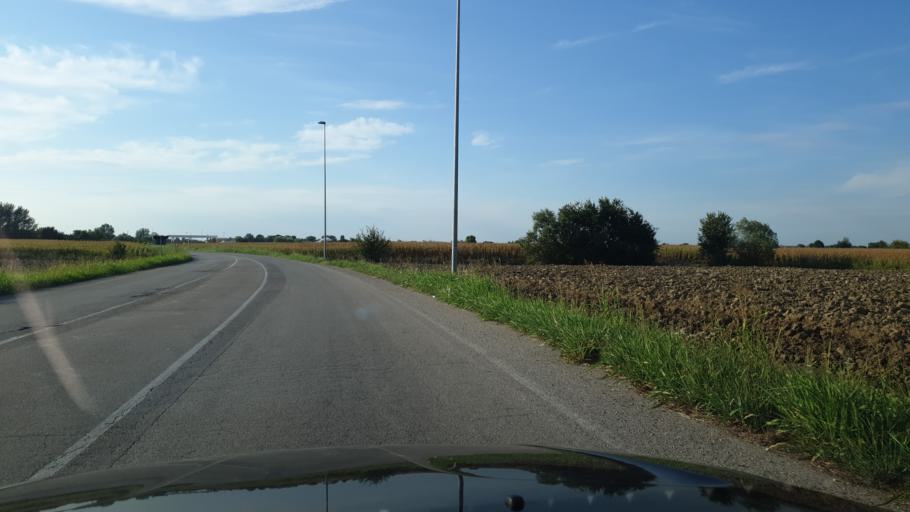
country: IT
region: Veneto
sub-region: Provincia di Rovigo
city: Fiesso Umbertiano
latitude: 44.9504
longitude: 11.6210
